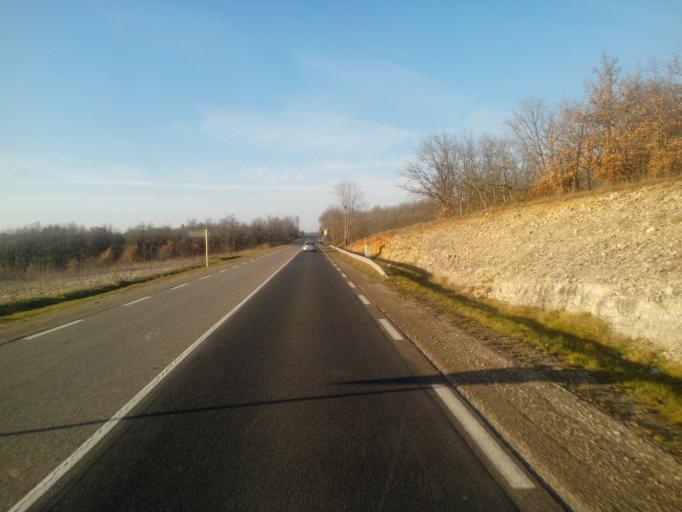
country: FR
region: Limousin
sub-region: Departement de la Correze
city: Brive-la-Gaillarde
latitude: 45.0379
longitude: 1.5035
